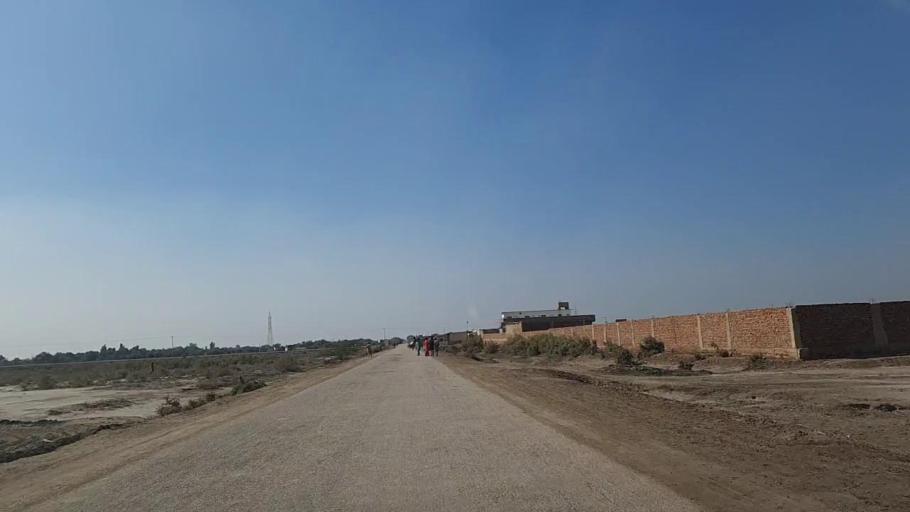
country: PK
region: Sindh
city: Daur
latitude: 26.3500
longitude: 68.3453
